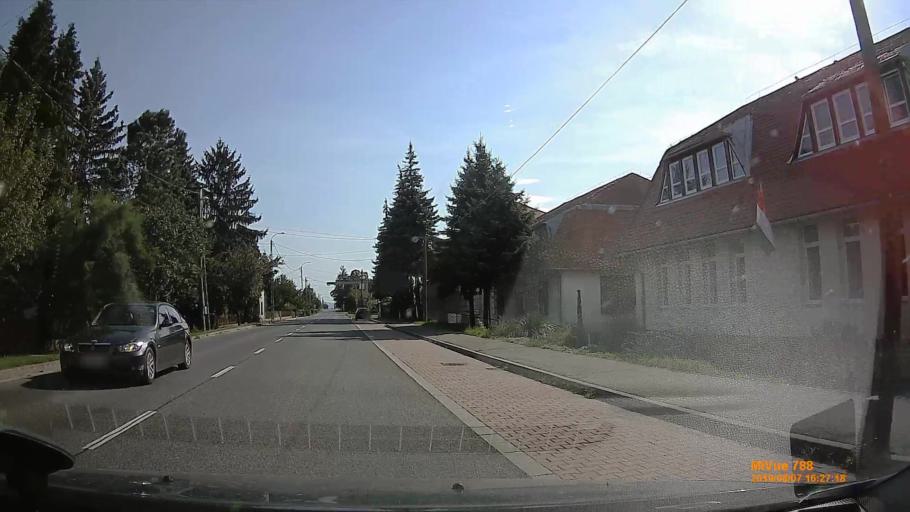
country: HU
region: Zala
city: Lenti
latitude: 46.7031
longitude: 16.5499
